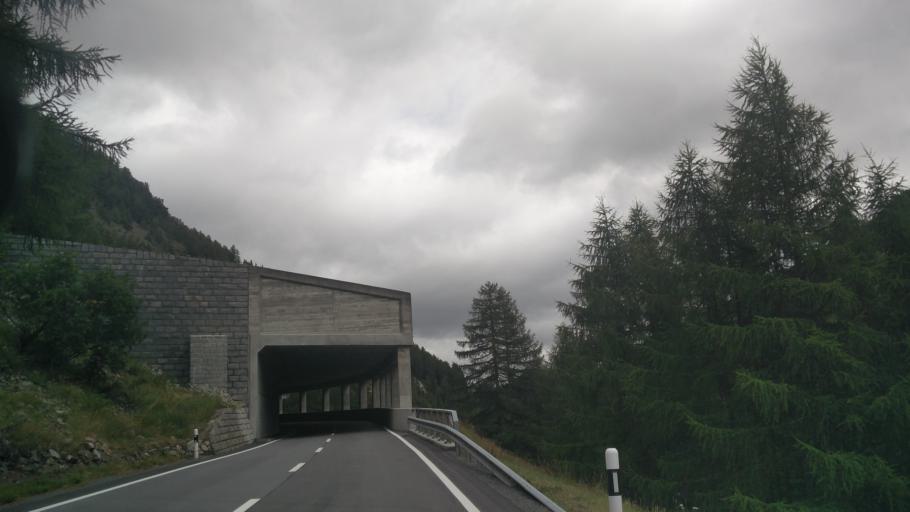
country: CH
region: Grisons
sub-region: Inn District
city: Zernez
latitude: 46.6979
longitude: 10.1097
